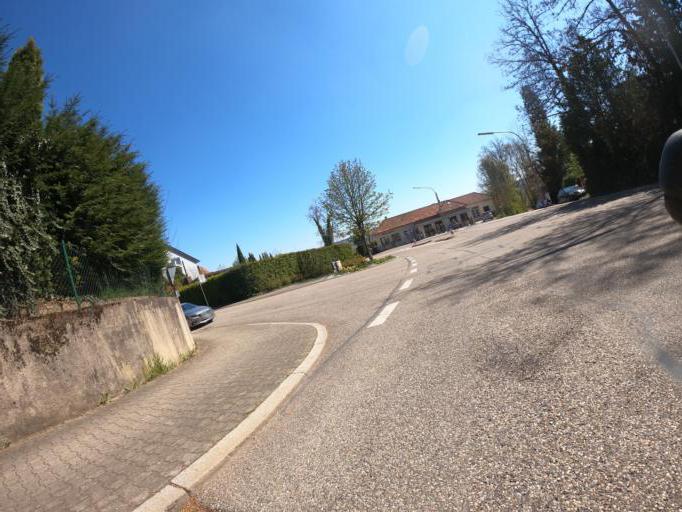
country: DE
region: Baden-Wuerttemberg
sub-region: Karlsruhe Region
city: Pforzheim
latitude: 48.9010
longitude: 8.7014
